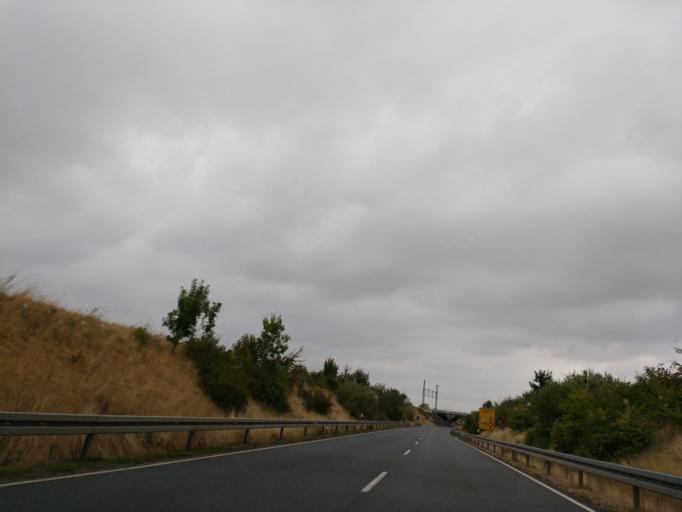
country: DE
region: Lower Saxony
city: Vechelde
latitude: 52.2606
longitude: 10.3495
